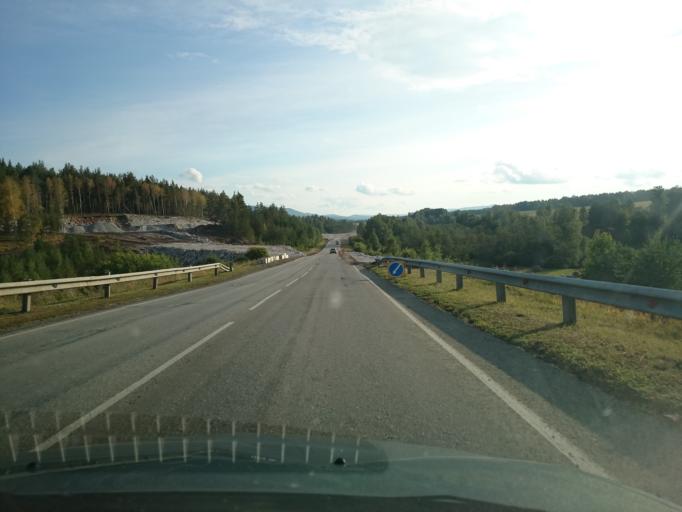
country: RU
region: Bashkortostan
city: Lomovka
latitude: 53.9131
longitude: 58.1819
